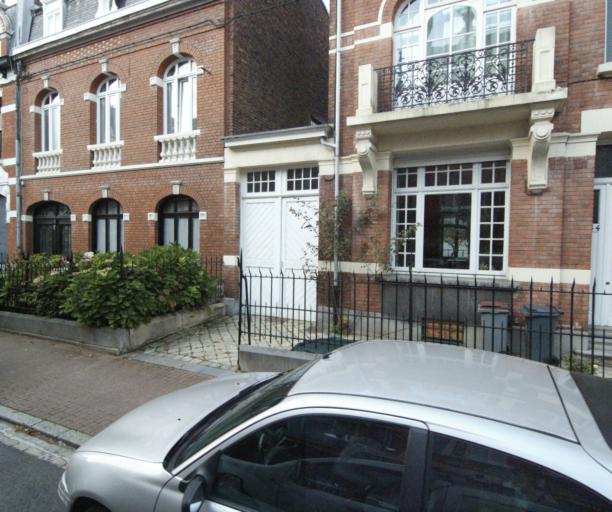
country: FR
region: Nord-Pas-de-Calais
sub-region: Departement du Nord
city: La Madeleine
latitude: 50.6411
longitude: 3.0890
